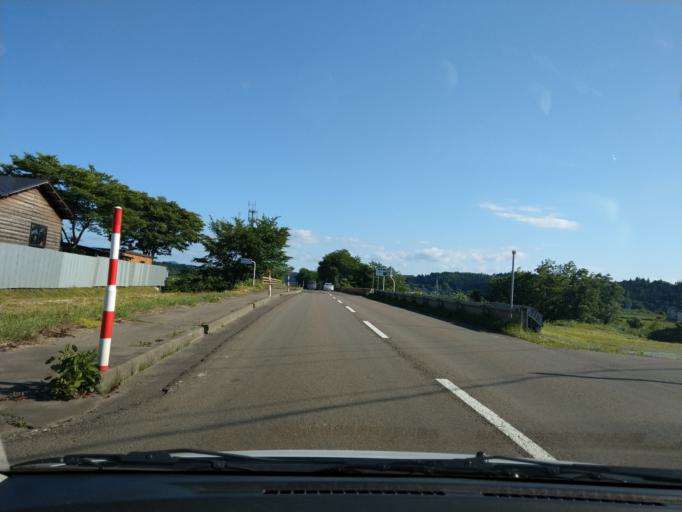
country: JP
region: Akita
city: Takanosu
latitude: 40.1989
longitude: 140.3962
